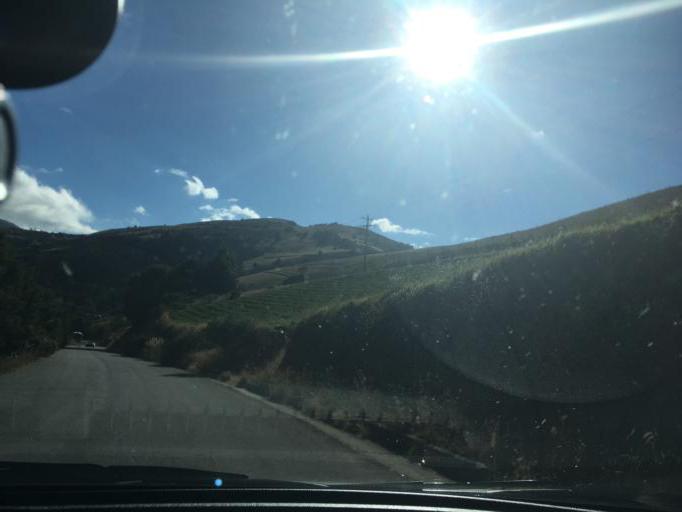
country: CO
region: Boyaca
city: Pesca
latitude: 5.5172
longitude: -72.9749
